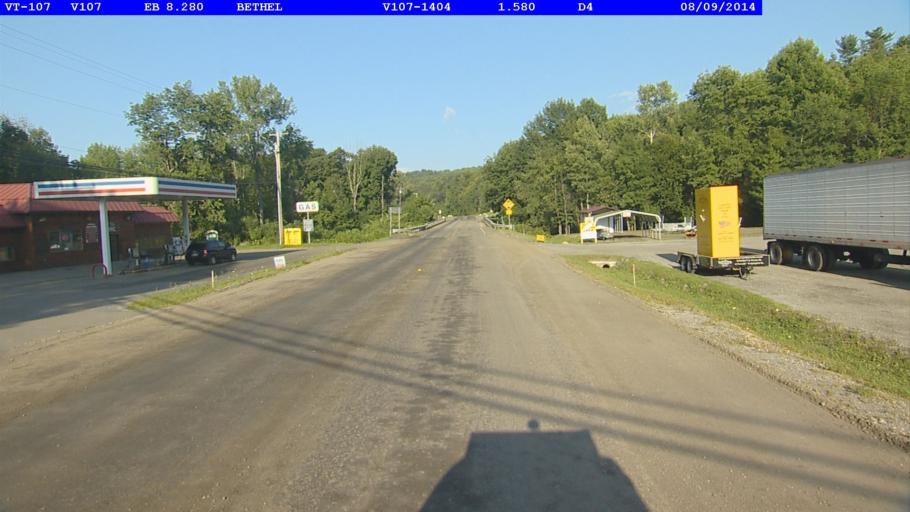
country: US
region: Vermont
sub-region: Orange County
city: Randolph
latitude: 43.8099
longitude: -72.6501
